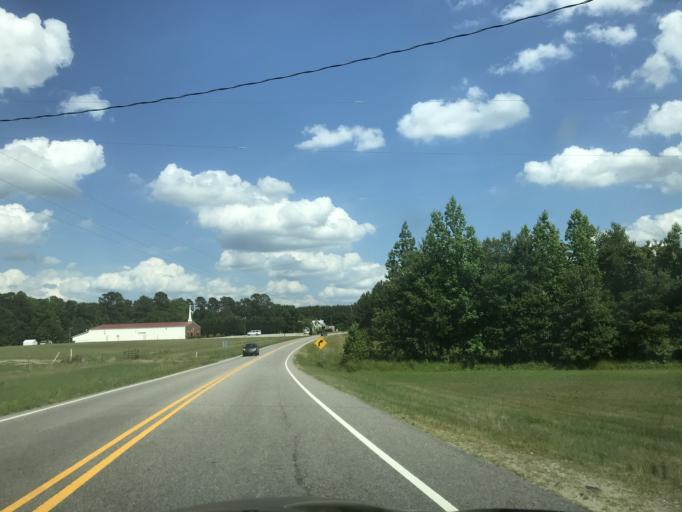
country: US
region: North Carolina
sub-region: Wake County
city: Rolesville
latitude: 35.9765
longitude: -78.3503
